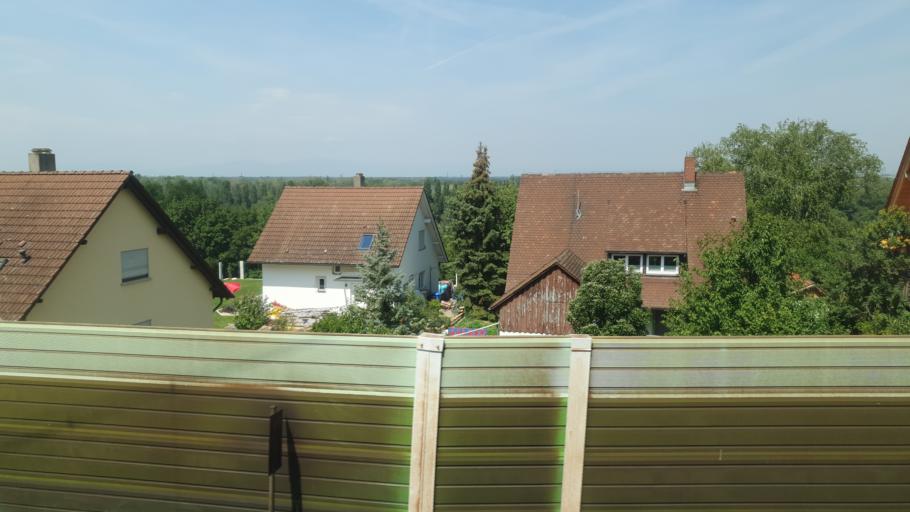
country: DE
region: Baden-Wuerttemberg
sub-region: Freiburg Region
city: Bad Bellingen
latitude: 47.7114
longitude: 7.5380
